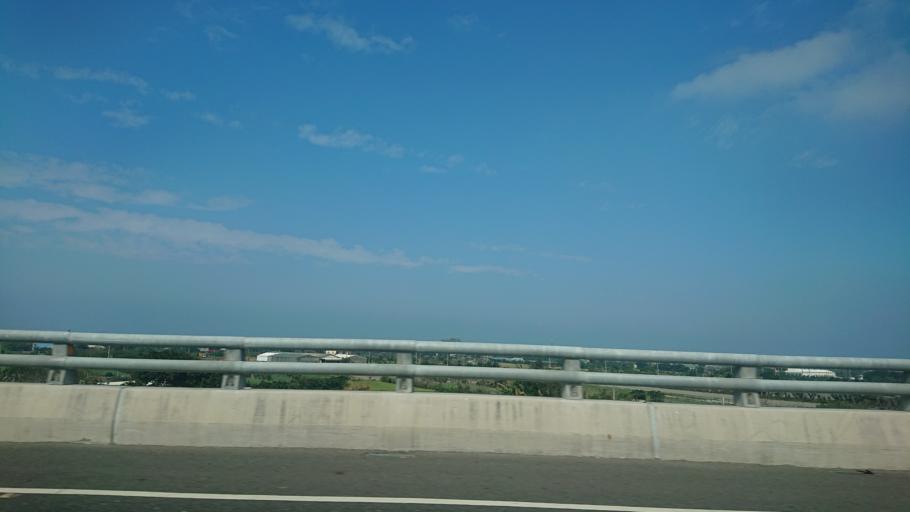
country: TW
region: Taiwan
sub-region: Changhua
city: Chang-hua
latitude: 23.9912
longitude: 120.3736
